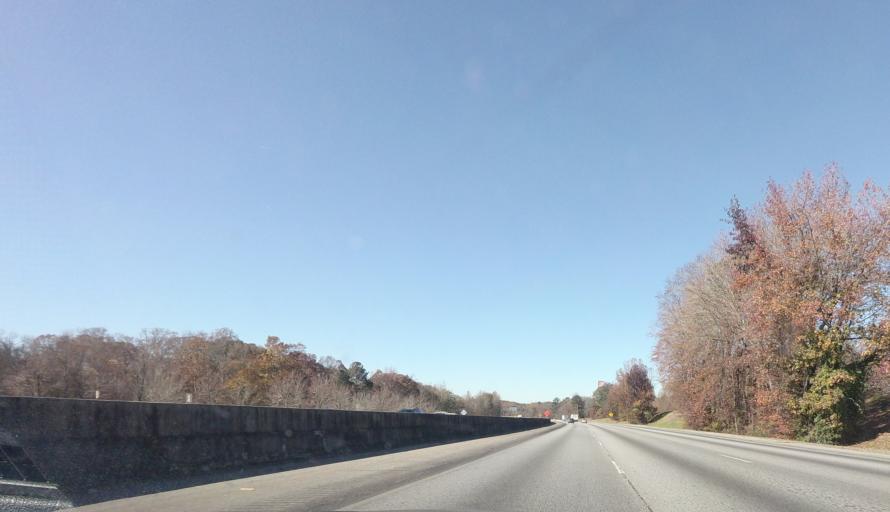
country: US
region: Georgia
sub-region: Cobb County
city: Austell
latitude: 33.7770
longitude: -84.6064
